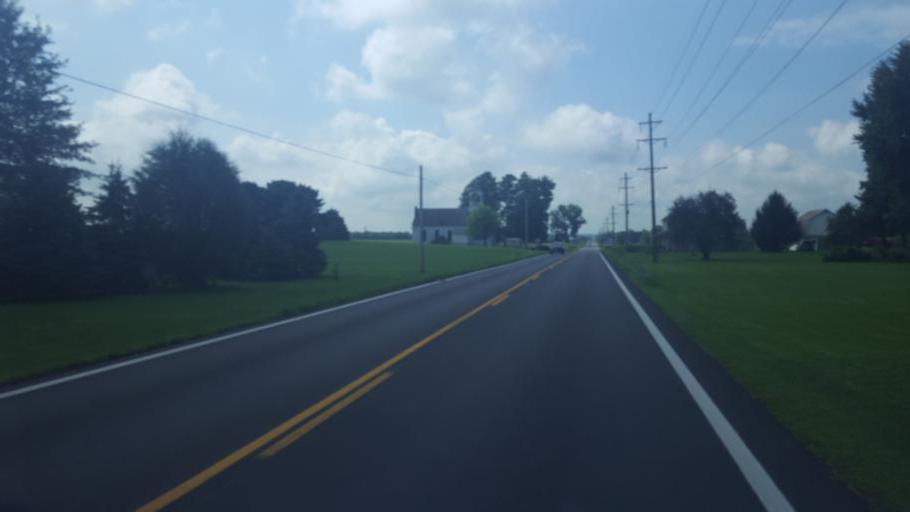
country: US
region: Ohio
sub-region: Fairfield County
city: Baltimore
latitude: 39.8704
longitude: -82.5661
